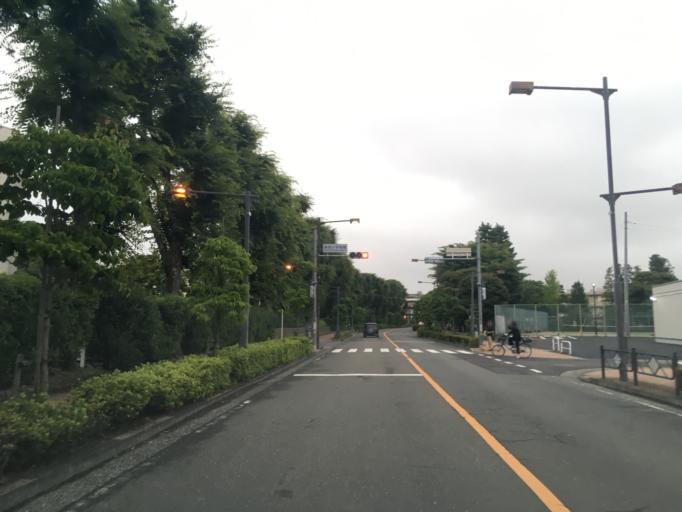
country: JP
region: Tokyo
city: Chofugaoka
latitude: 35.6405
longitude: 139.5596
